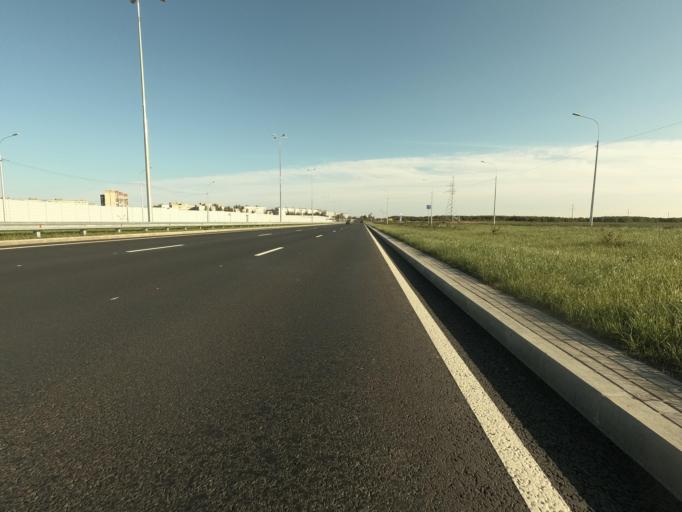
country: RU
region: St.-Petersburg
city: Kolpino
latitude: 59.7393
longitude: 30.5503
